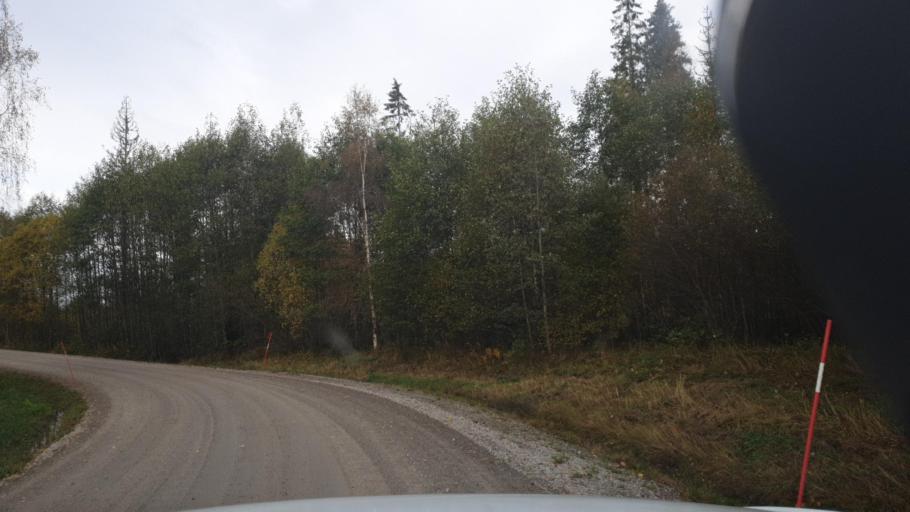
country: SE
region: Vaermland
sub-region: Arvika Kommun
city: Arvika
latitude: 59.7095
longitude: 12.8533
